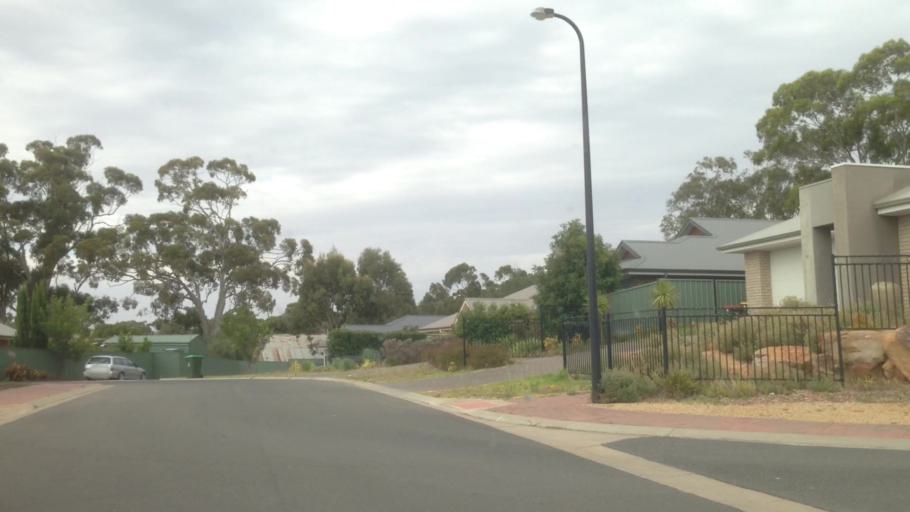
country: AU
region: South Australia
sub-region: Barossa
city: Williamstown
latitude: -34.6723
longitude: 138.8879
